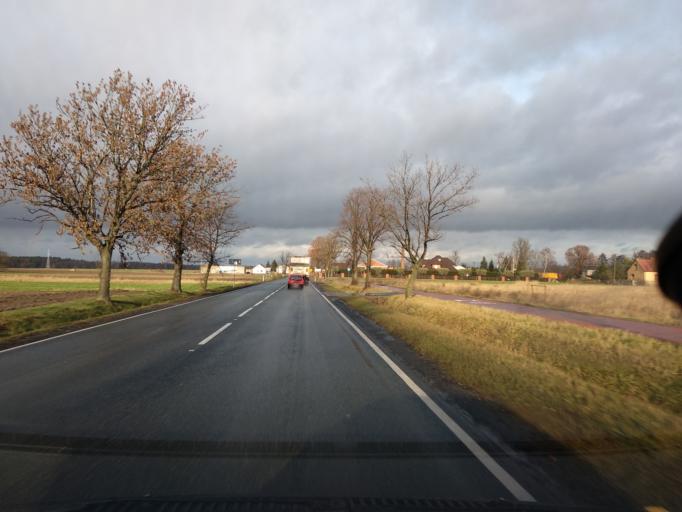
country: PL
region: Greater Poland Voivodeship
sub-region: Powiat koninski
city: Rychwal
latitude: 52.1128
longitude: 18.1676
